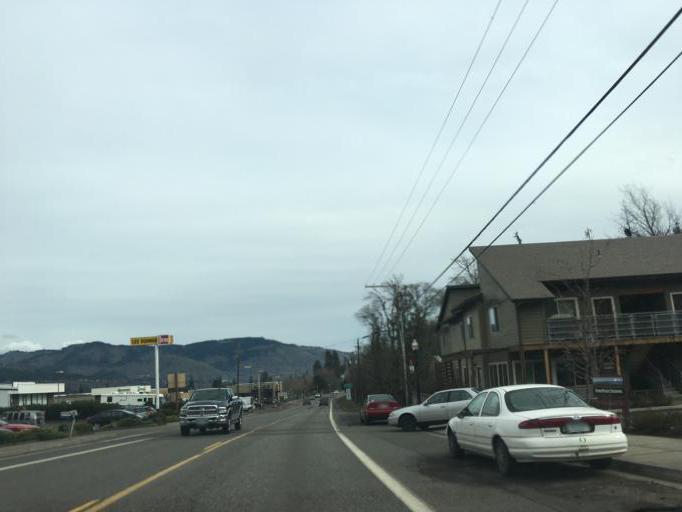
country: US
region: Oregon
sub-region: Hood River County
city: Hood River
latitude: 45.7108
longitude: -121.5443
